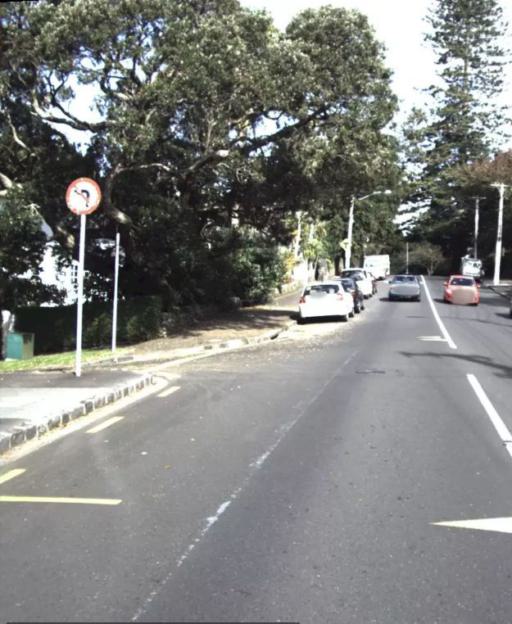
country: NZ
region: Auckland
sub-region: Auckland
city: Auckland
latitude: -36.8771
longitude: 174.7706
